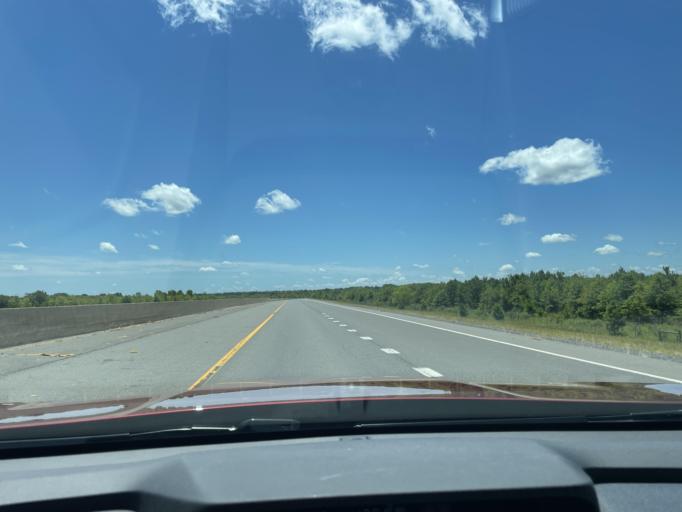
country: US
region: Arkansas
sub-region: Jefferson County
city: Pine Bluff
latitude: 34.1670
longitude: -91.9857
